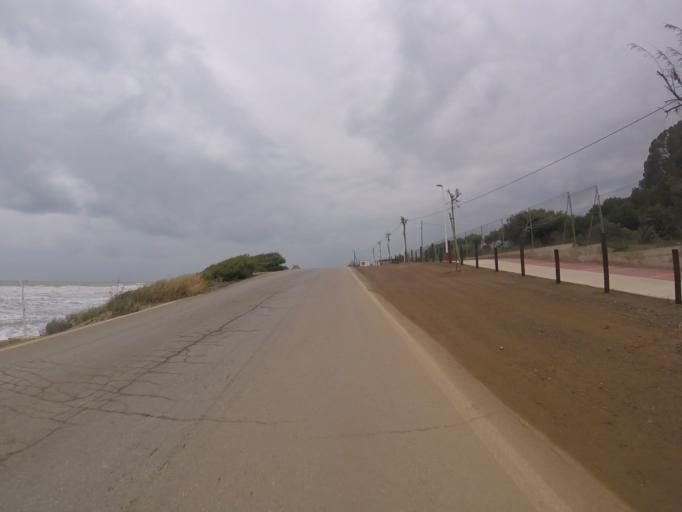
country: ES
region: Valencia
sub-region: Provincia de Castello
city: Alcoceber
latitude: 40.2237
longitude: 0.2704
